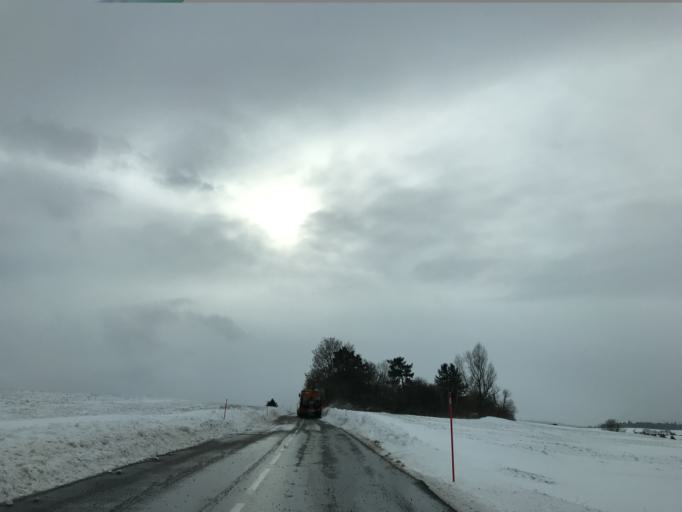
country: FR
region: Auvergne
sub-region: Departement du Puy-de-Dome
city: Aydat
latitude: 45.6603
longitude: 2.9225
